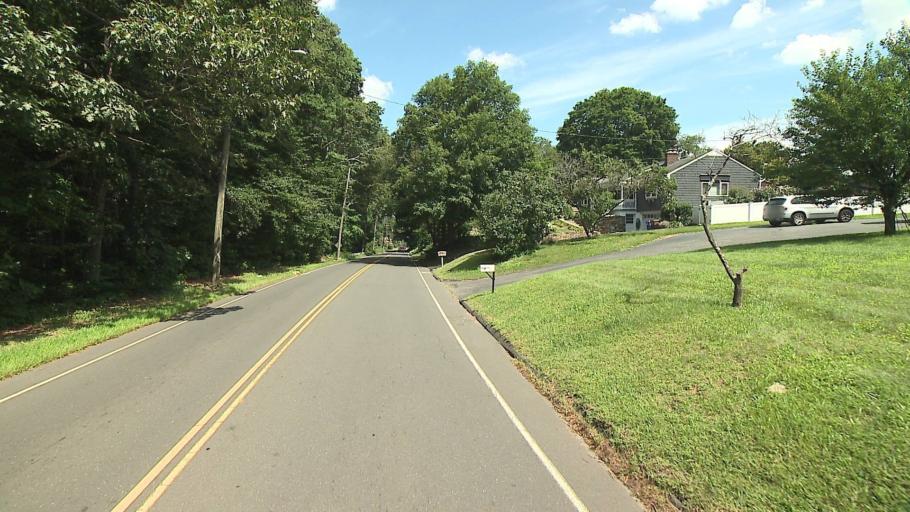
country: US
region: Connecticut
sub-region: Fairfield County
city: Shelton
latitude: 41.3190
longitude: -73.1086
